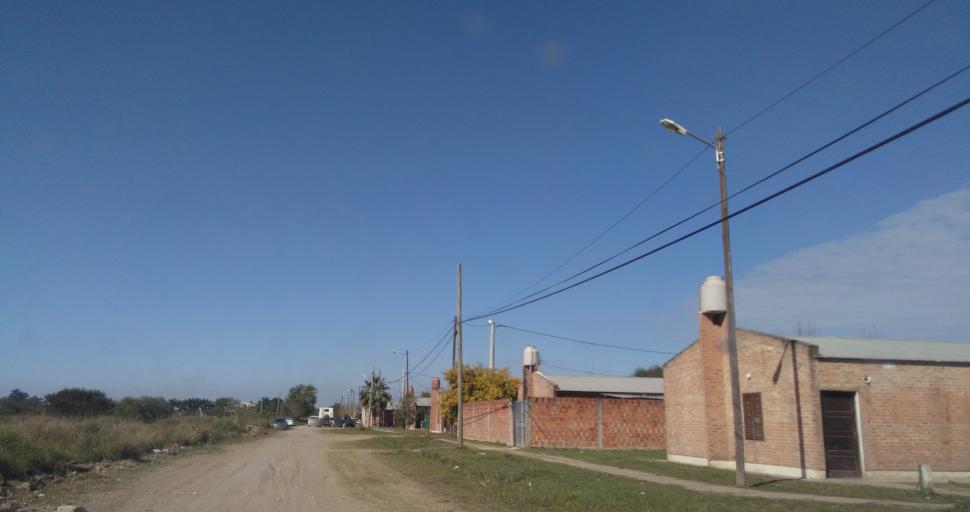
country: AR
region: Chaco
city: Fontana
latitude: -27.4575
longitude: -59.0428
